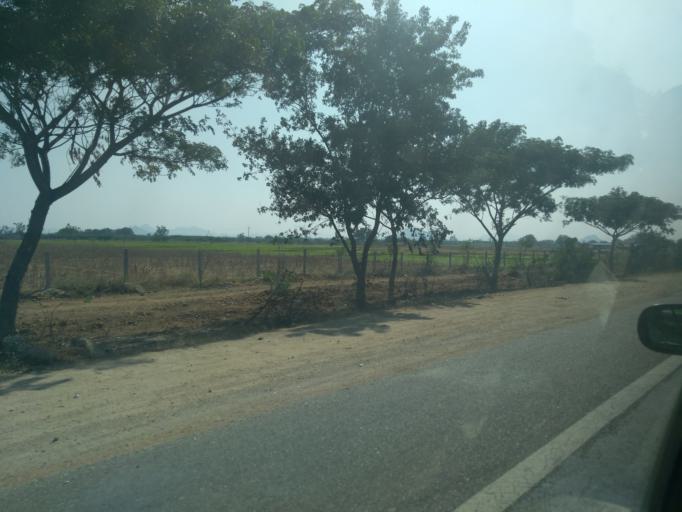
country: IN
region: Telangana
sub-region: Mahbubnagar
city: Mahbubnagar
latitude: 16.6775
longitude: 78.0284
